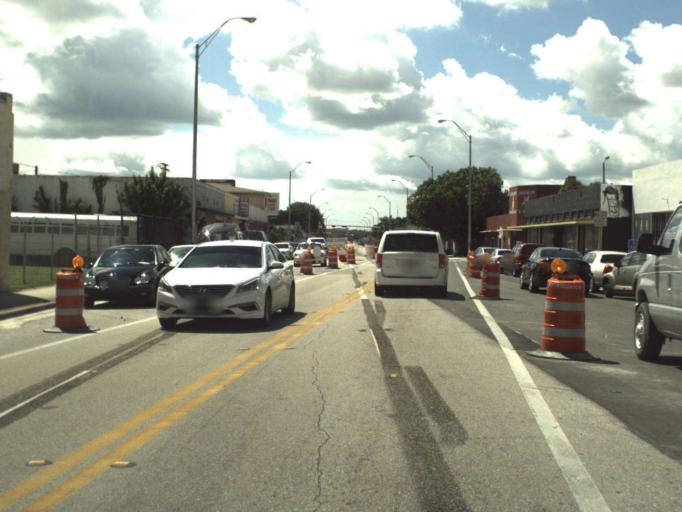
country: US
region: Florida
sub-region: Miami-Dade County
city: Allapattah
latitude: 25.8279
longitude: -80.2083
